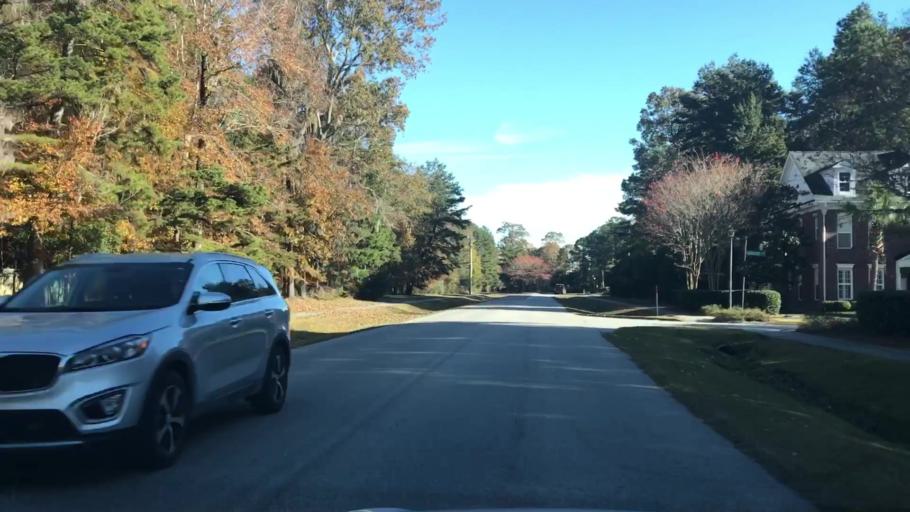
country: US
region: South Carolina
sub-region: Charleston County
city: Shell Point
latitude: 32.8366
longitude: -80.0898
